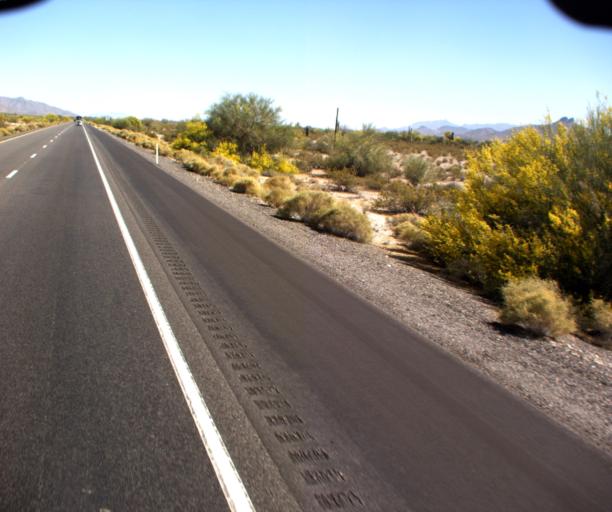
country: US
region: Arizona
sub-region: Maricopa County
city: Gila Bend
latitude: 32.8966
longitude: -112.5032
